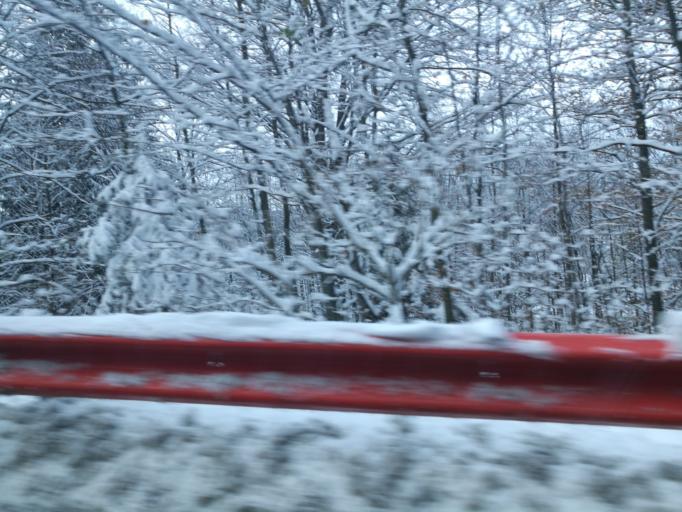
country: RO
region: Brasov
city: Brasov
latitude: 45.6016
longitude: 25.5527
